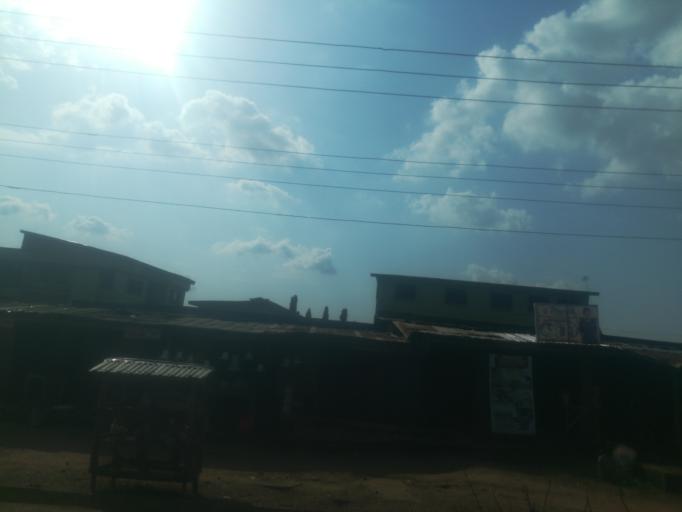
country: NG
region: Oyo
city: Moniya
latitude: 7.5114
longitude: 3.9126
